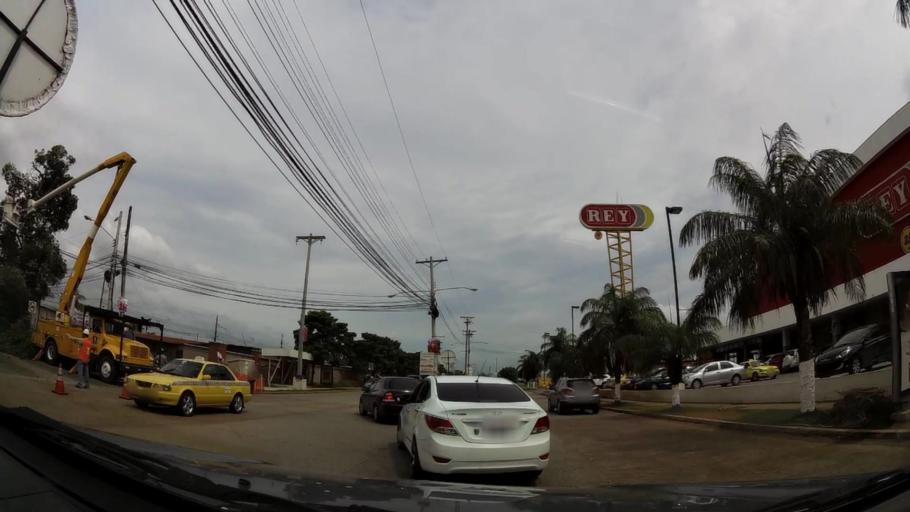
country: PA
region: Panama
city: San Miguelito
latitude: 9.0434
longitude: -79.4165
